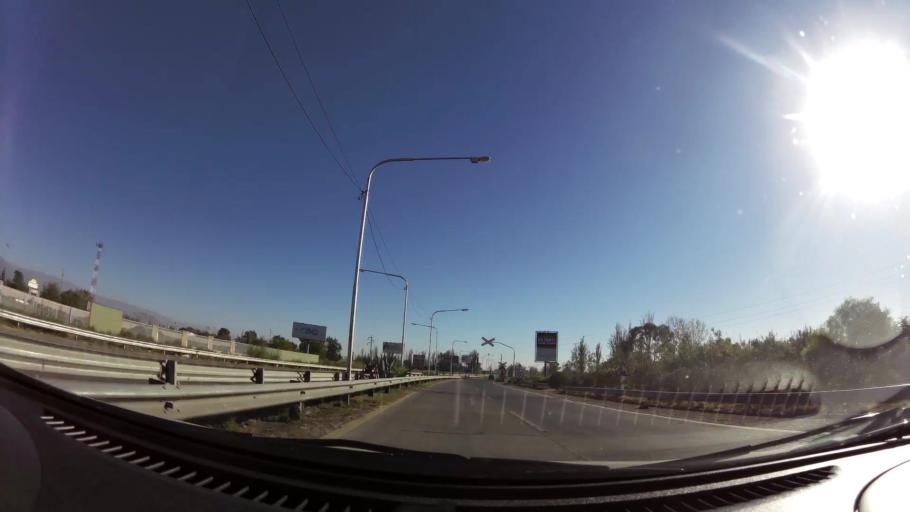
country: AR
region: Mendoza
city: Las Heras
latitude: -32.8312
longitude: -68.8065
